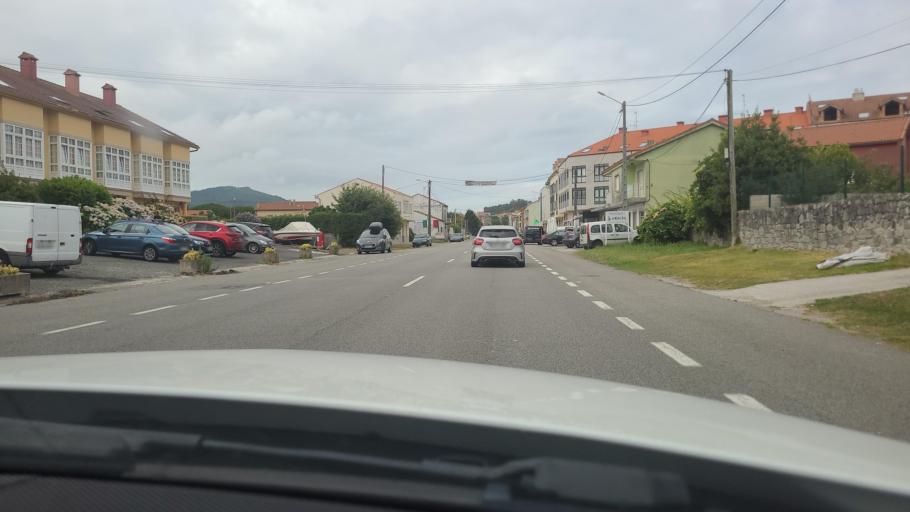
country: ES
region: Galicia
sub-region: Provincia da Coruna
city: Fisterra
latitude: 42.9247
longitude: -9.2615
